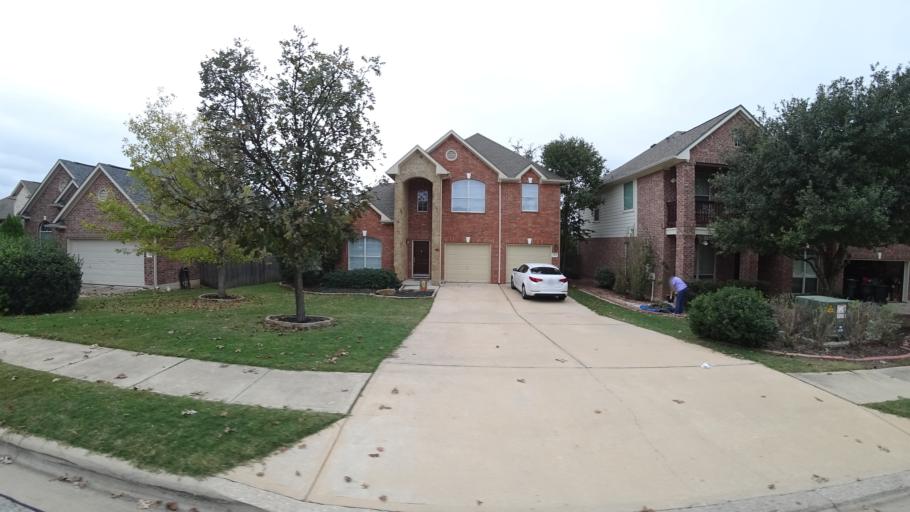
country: US
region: Texas
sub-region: Travis County
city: Bee Cave
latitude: 30.3537
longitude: -97.9071
